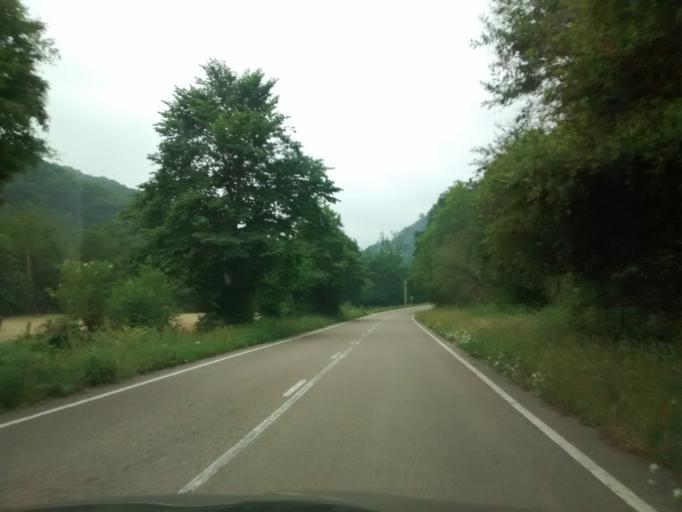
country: ES
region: Cantabria
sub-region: Provincia de Cantabria
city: Ruente
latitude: 43.1490
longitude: -4.2158
